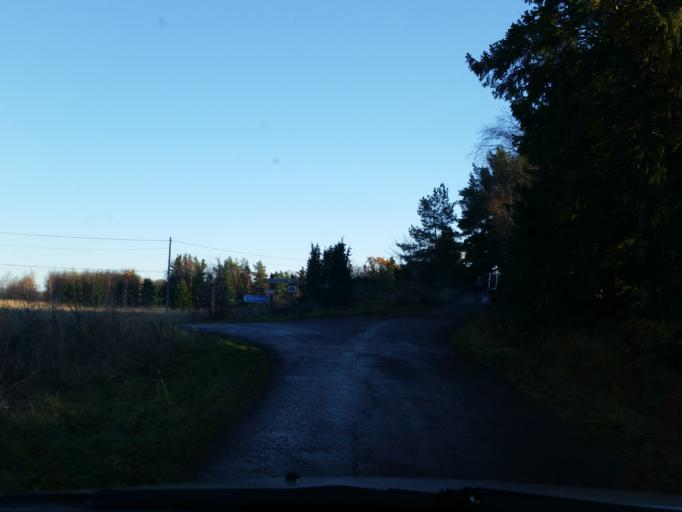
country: AX
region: Alands skaergard
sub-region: Braendoe
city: Braendoe
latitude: 60.3570
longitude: 21.0687
